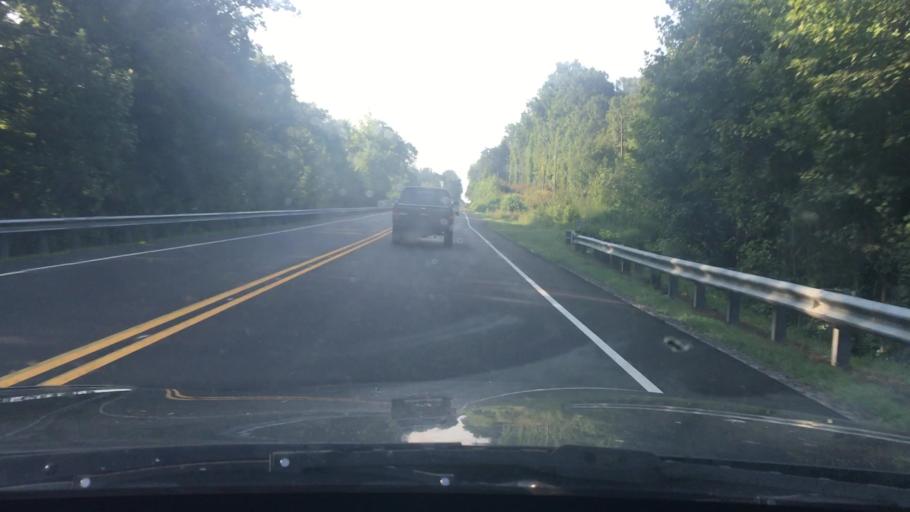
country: US
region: North Carolina
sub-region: Caswell County
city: Yanceyville
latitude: 36.4412
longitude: -79.3632
